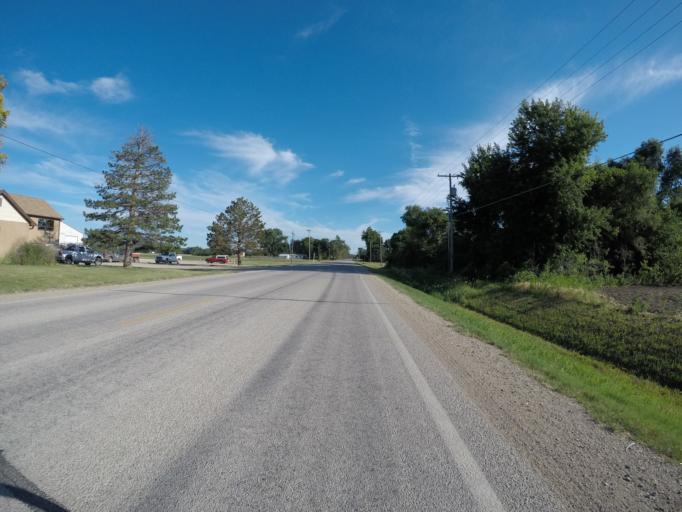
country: US
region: Kansas
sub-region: Riley County
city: Manhattan
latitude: 39.1650
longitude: -96.5771
